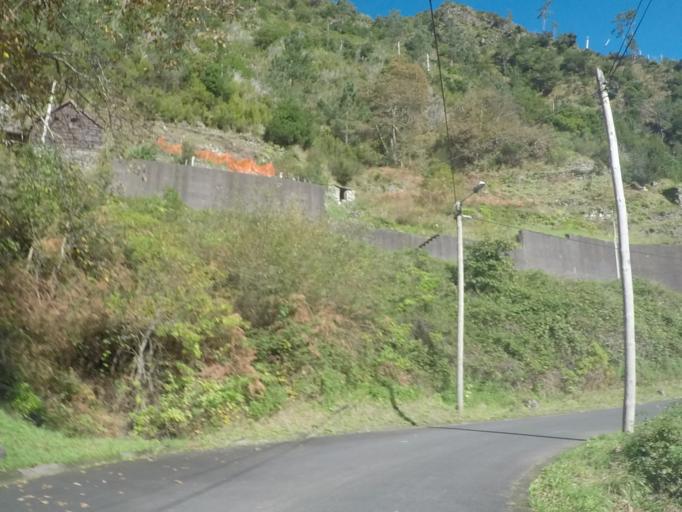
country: PT
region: Madeira
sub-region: Camara de Lobos
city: Curral das Freiras
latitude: 32.7843
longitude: -16.9776
